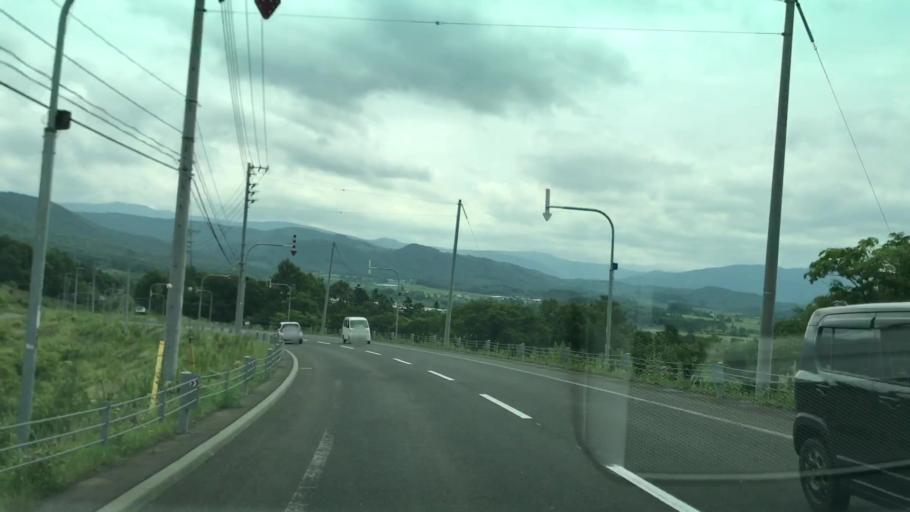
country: JP
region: Hokkaido
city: Yoichi
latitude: 43.1096
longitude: 140.8197
